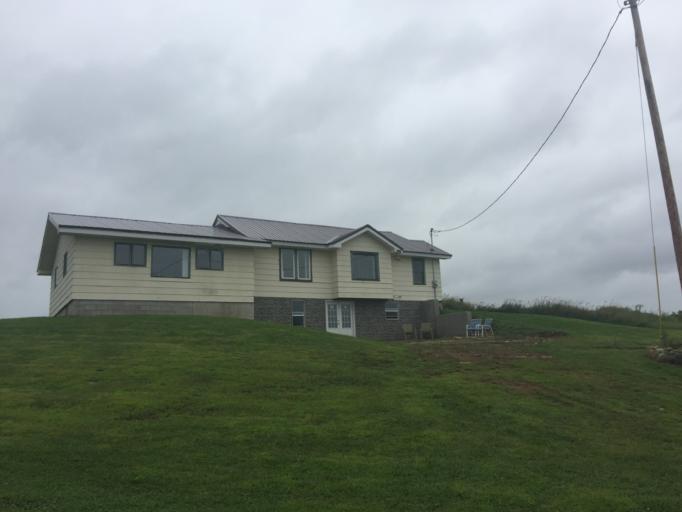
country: US
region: Wisconsin
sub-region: Oconto County
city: Oconto
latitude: 44.9325
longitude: -87.9894
